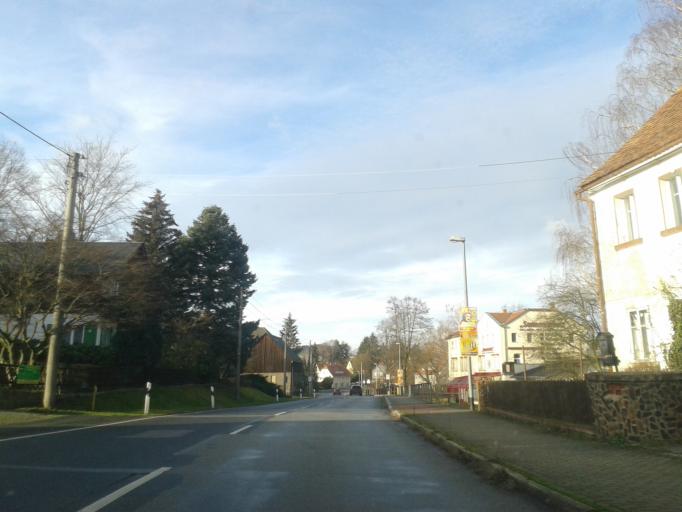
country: DE
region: Saxony
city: Eibau
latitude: 50.9742
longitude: 14.6724
